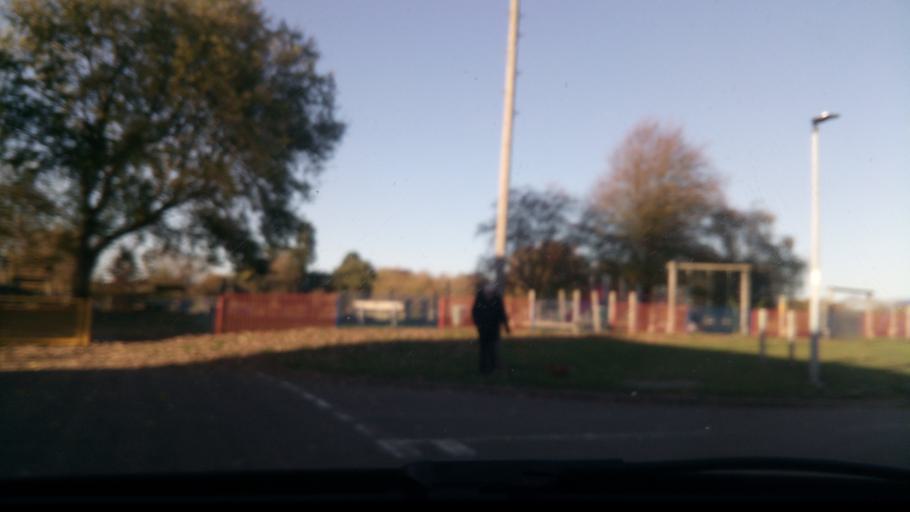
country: GB
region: England
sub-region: Peterborough
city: Wittering
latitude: 52.6078
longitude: -0.4423
